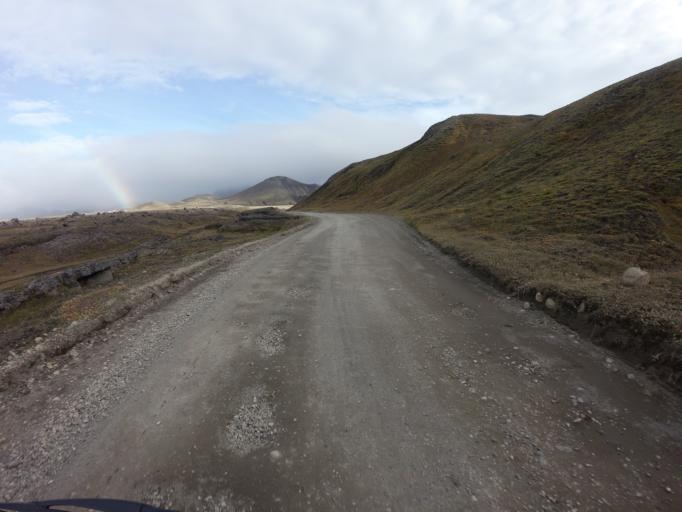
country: IS
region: South
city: Vestmannaeyjar
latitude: 64.0064
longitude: -19.0397
